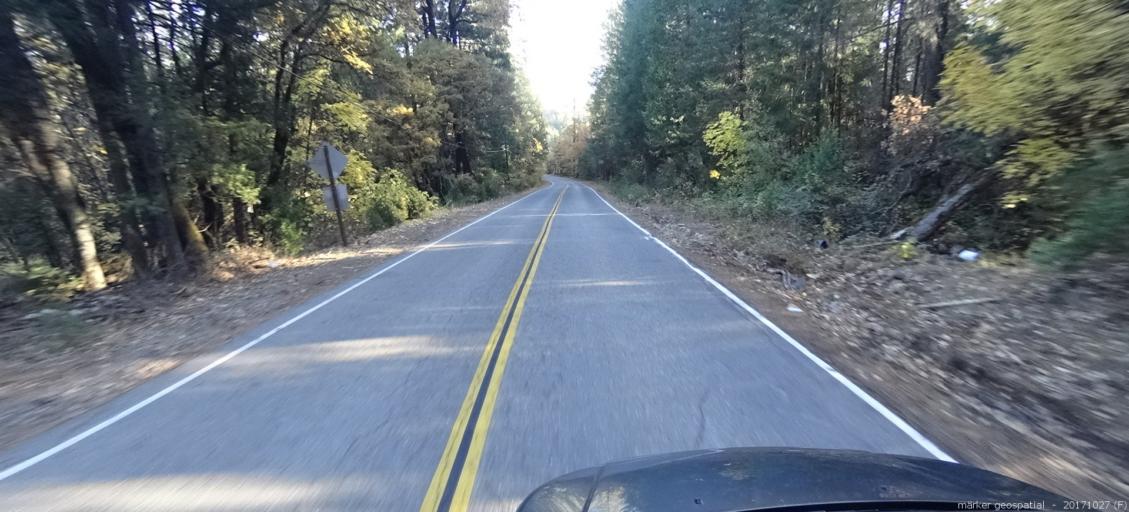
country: US
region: California
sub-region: Shasta County
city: Burney
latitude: 41.0097
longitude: -121.9084
